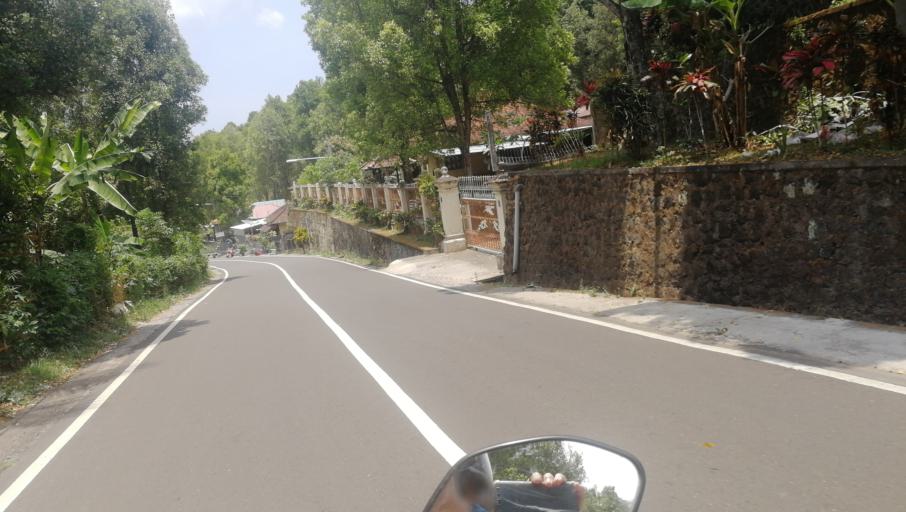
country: ID
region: Bali
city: Banjar Pedawa
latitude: -8.2634
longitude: 115.0366
